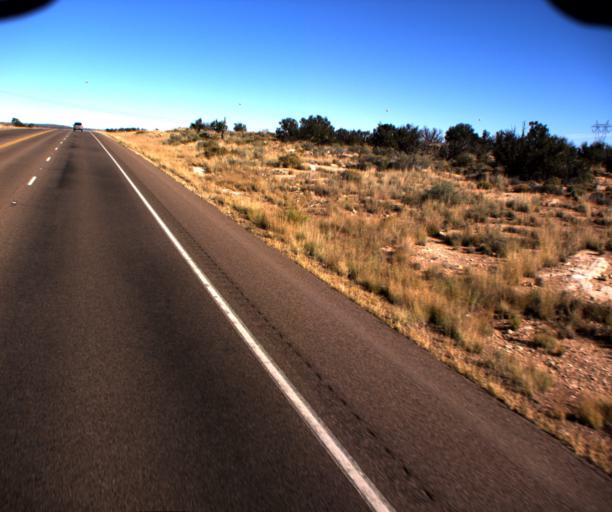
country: US
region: Arizona
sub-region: Navajo County
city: Snowflake
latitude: 34.6295
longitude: -110.0938
